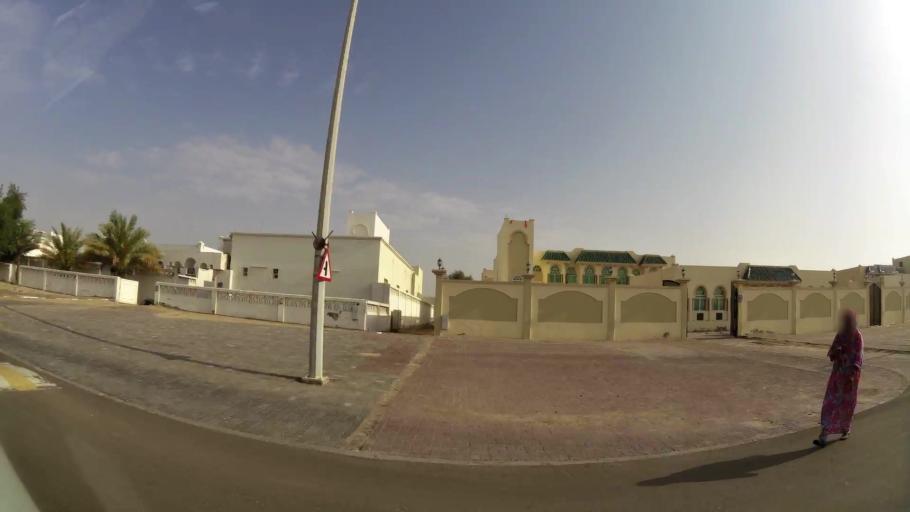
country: AE
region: Abu Dhabi
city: Abu Dhabi
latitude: 24.2594
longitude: 54.6717
